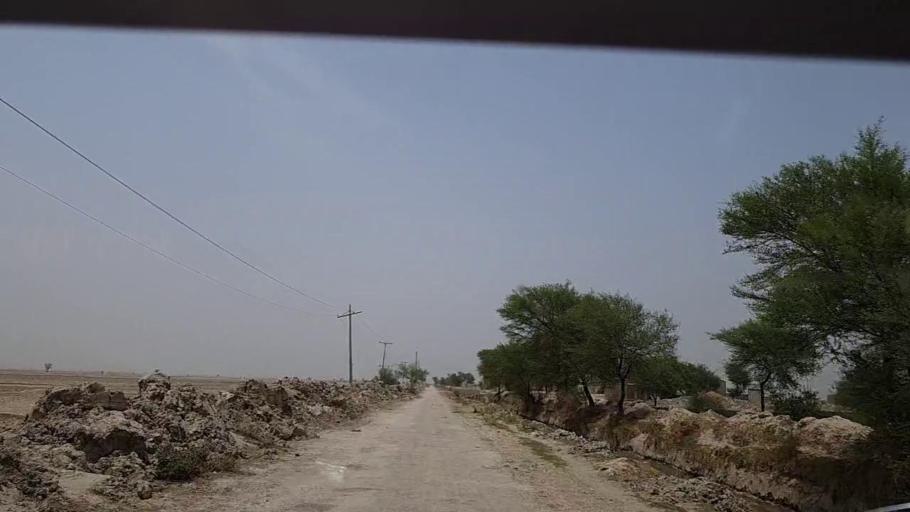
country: PK
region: Sindh
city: Khairpur Nathan Shah
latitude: 27.0455
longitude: 67.6189
